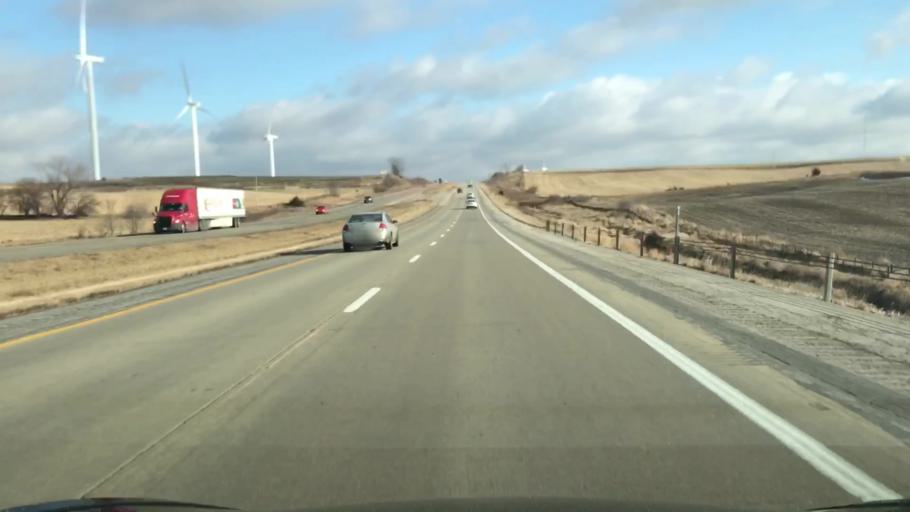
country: US
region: Iowa
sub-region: Guthrie County
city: Guthrie Center
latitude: 41.4968
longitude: -94.7036
